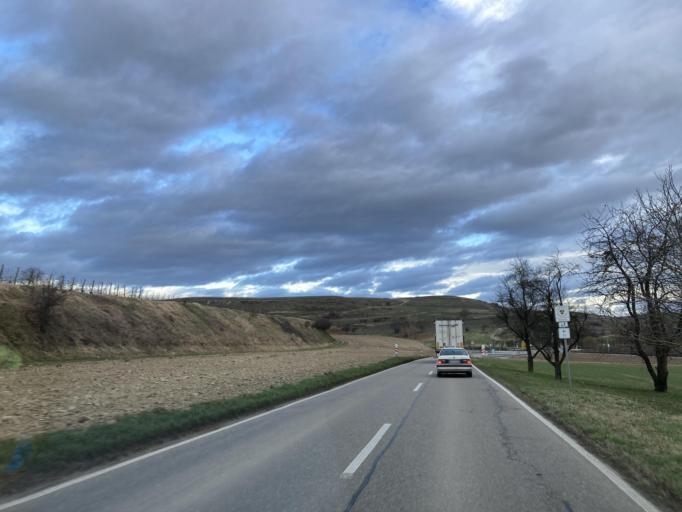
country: DE
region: Baden-Wuerttemberg
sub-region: Freiburg Region
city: Sasbach
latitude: 48.1115
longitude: 7.6150
